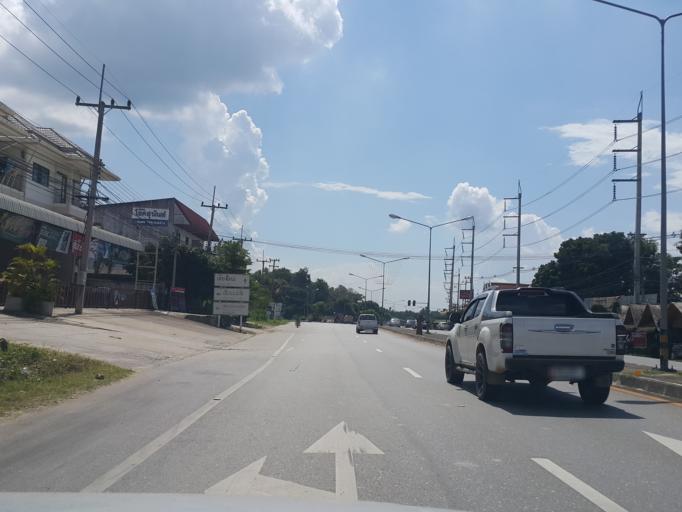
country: TH
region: Chiang Mai
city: Mae Taeng
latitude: 19.1332
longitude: 98.9490
